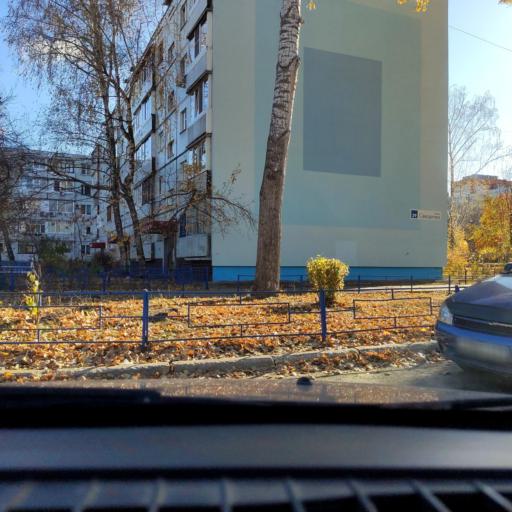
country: RU
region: Samara
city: Tol'yatti
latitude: 53.5273
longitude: 49.2838
